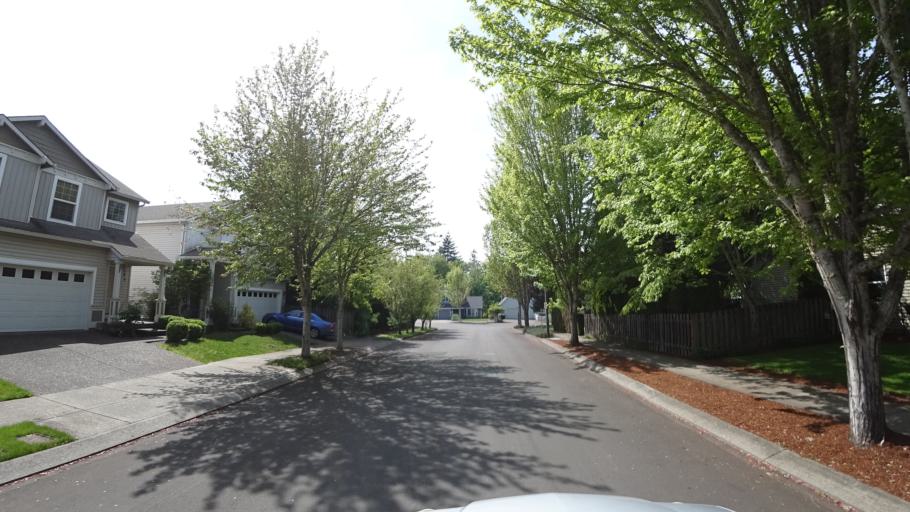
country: US
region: Oregon
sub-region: Washington County
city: Hillsboro
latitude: 45.5215
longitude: -122.9318
